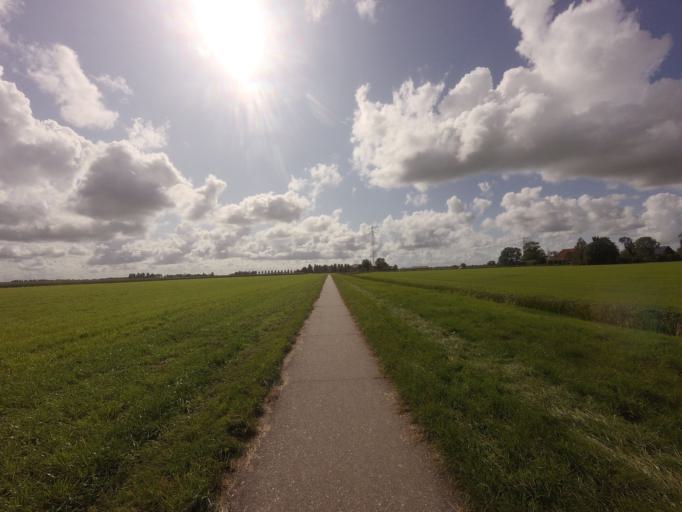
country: NL
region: Friesland
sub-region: Sudwest Fryslan
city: Sneek
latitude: 53.0643
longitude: 5.6352
